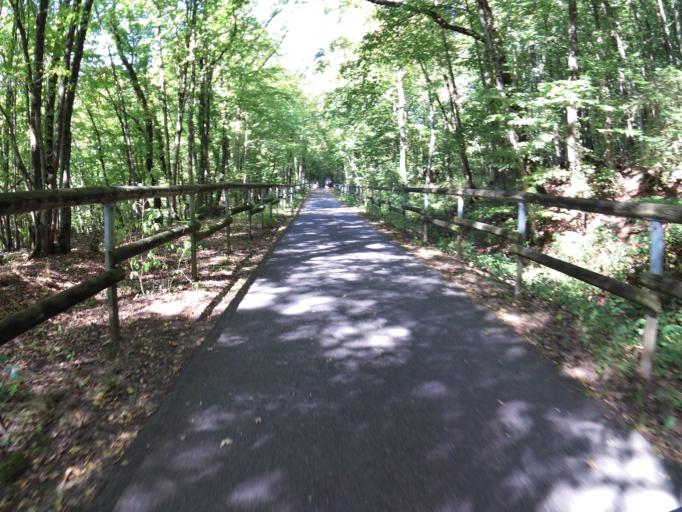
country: LU
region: Grevenmacher
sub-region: Canton d'Echternach
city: Rosport
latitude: 49.7718
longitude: 6.5147
